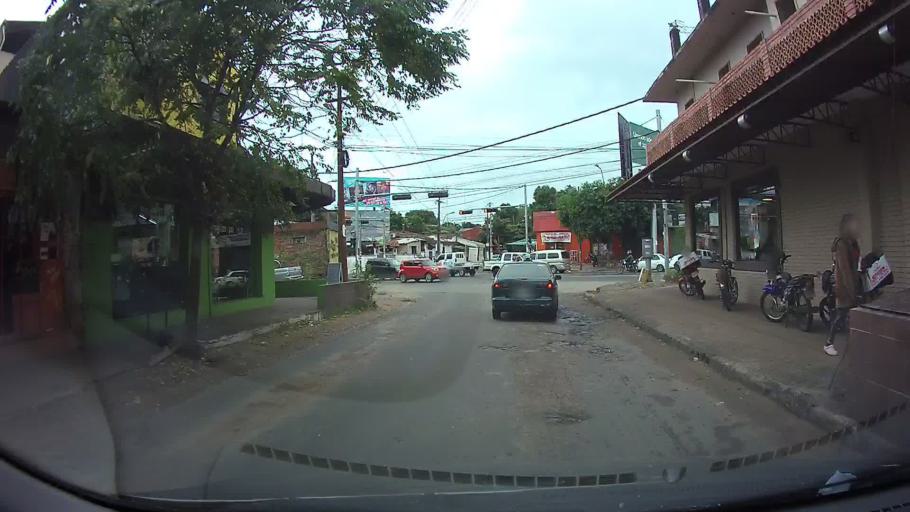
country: PY
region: Central
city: Lambare
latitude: -25.3175
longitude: -57.6076
